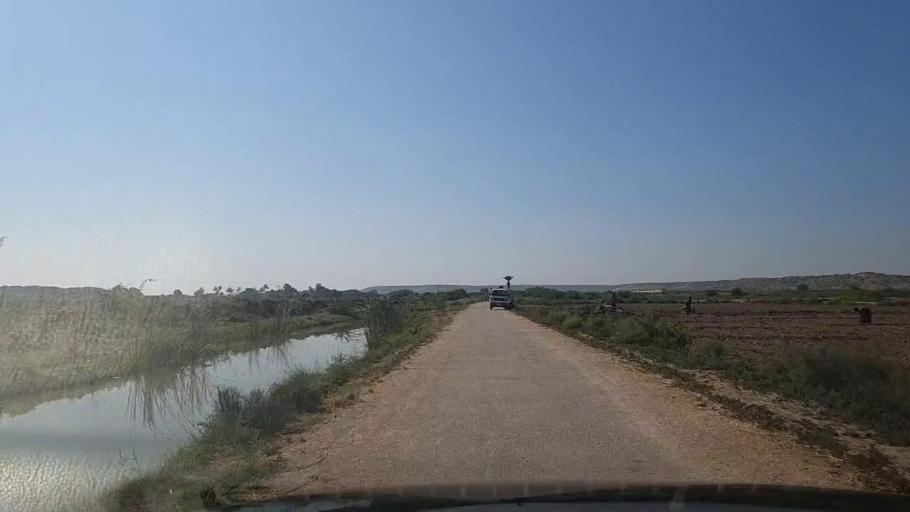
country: PK
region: Sindh
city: Thatta
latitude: 24.6311
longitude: 67.8713
